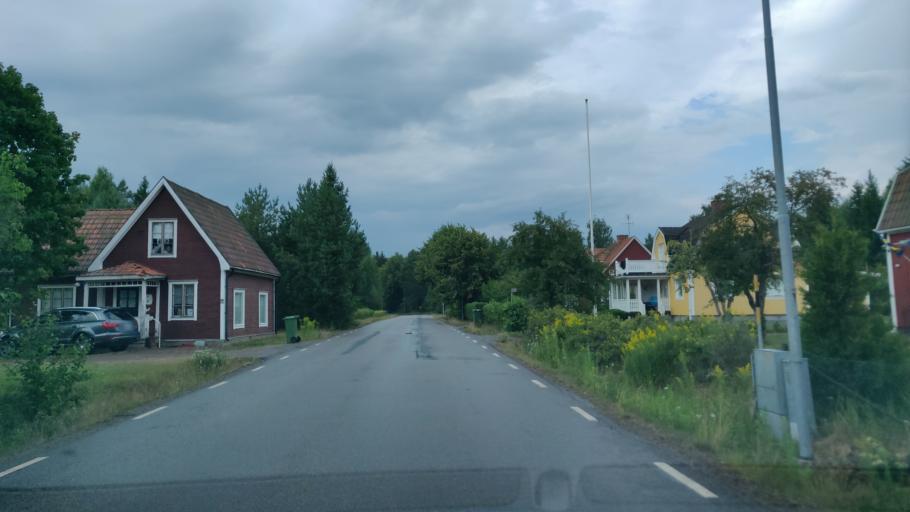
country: SE
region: Vaermland
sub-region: Munkfors Kommun
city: Munkfors
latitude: 59.8571
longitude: 13.5529
